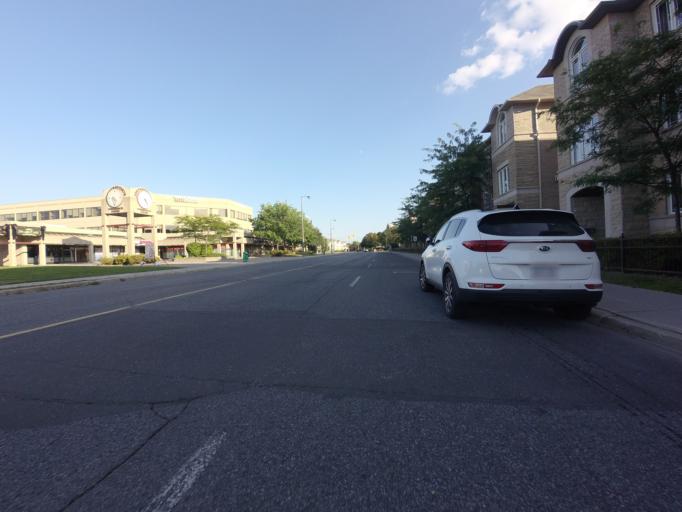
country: CA
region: Ontario
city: Bells Corners
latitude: 45.3431
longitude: -75.7635
